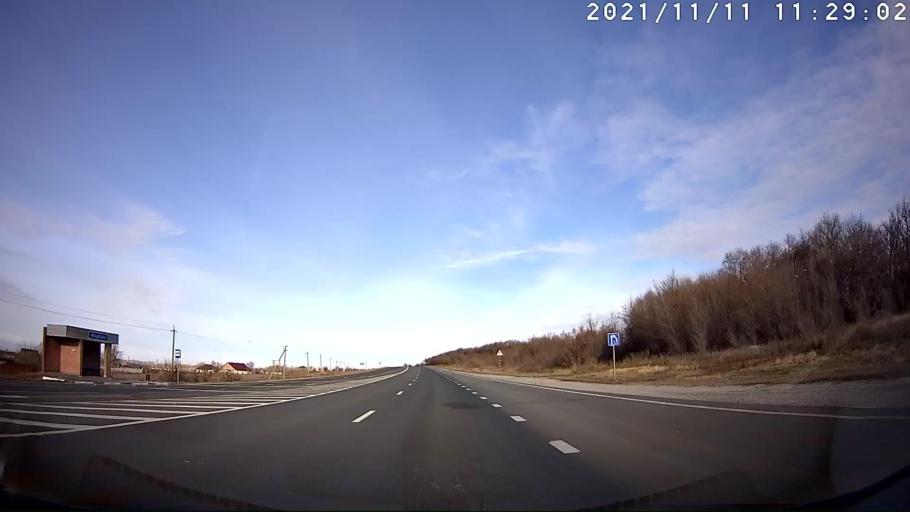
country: RU
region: Samara
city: Varlamovo
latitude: 53.2689
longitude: 48.4804
